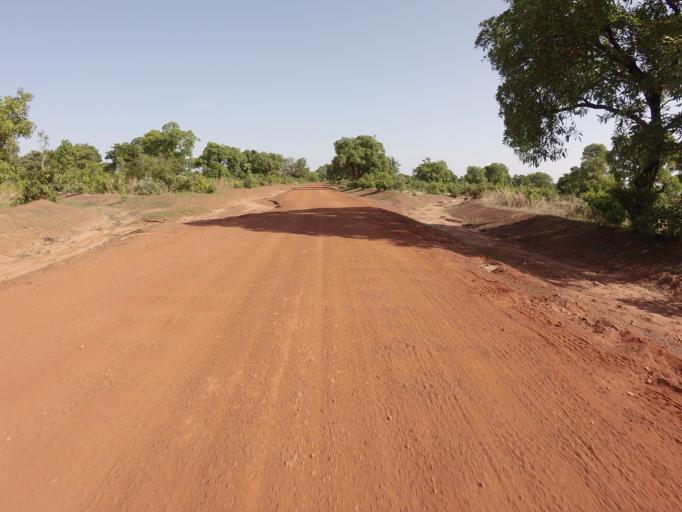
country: GH
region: Upper East
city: Bawku
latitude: 10.7424
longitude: -0.2004
